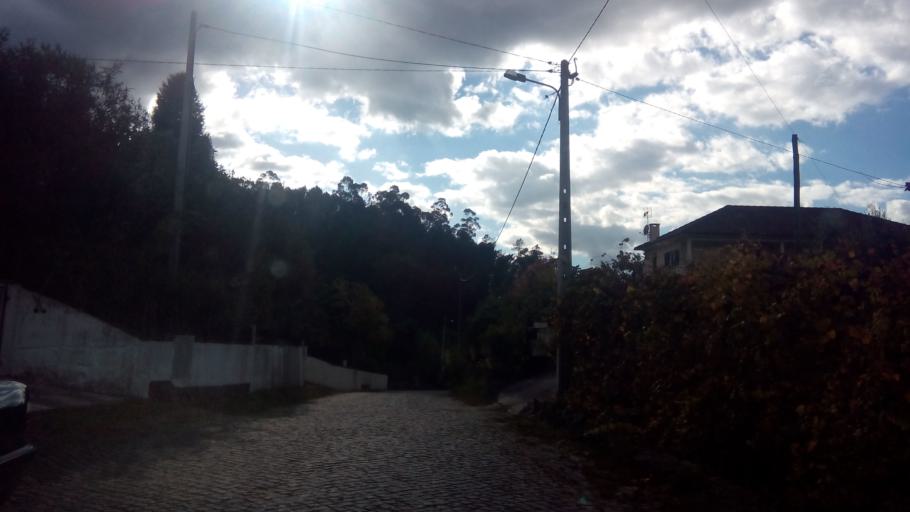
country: PT
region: Porto
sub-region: Amarante
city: Amarante
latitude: 41.2728
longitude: -7.9971
